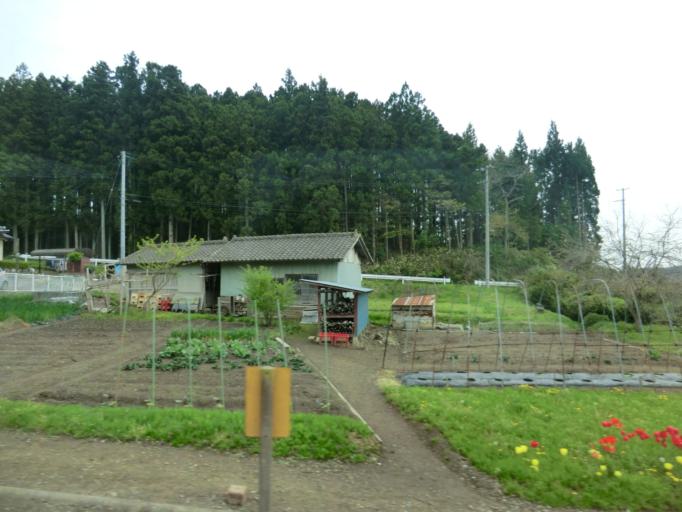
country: JP
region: Iwate
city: Ofunato
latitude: 38.9909
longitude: 141.7124
